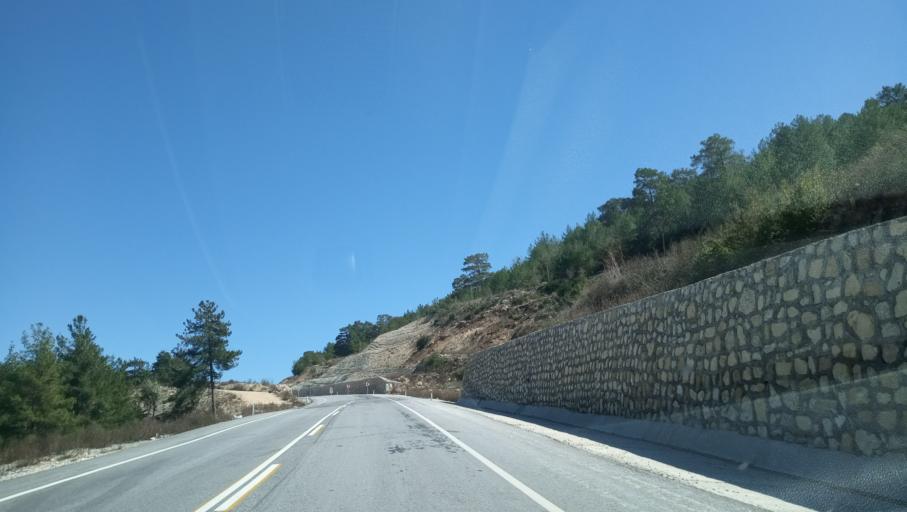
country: TR
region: Antalya
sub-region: Alanya
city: Okurcalar
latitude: 36.7752
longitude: 31.7571
